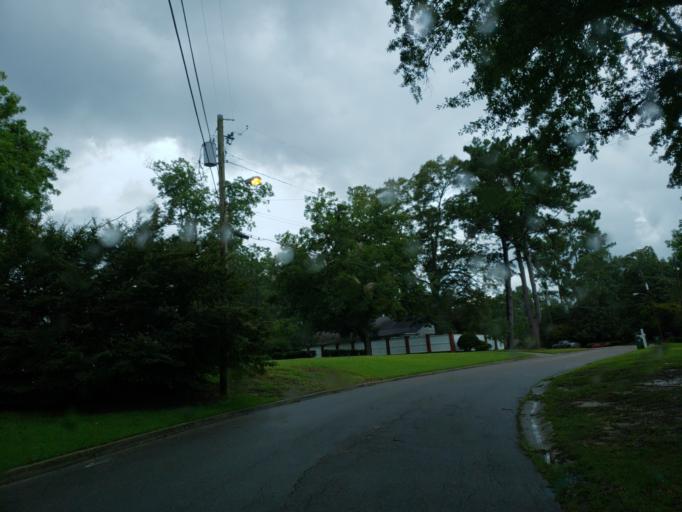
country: US
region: Mississippi
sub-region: Lamar County
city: West Hattiesburg
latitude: 31.3143
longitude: -89.3325
